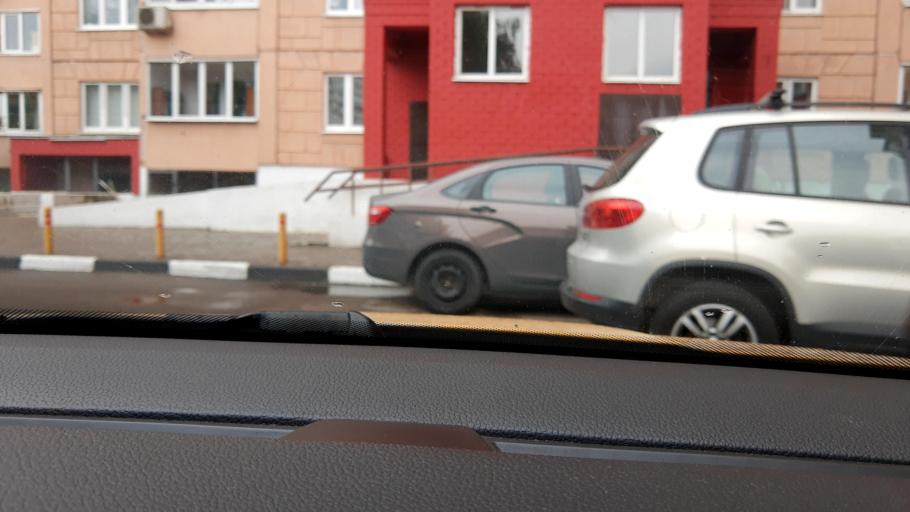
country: RU
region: Moscow
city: Vatutino
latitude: 55.9060
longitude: 37.7004
